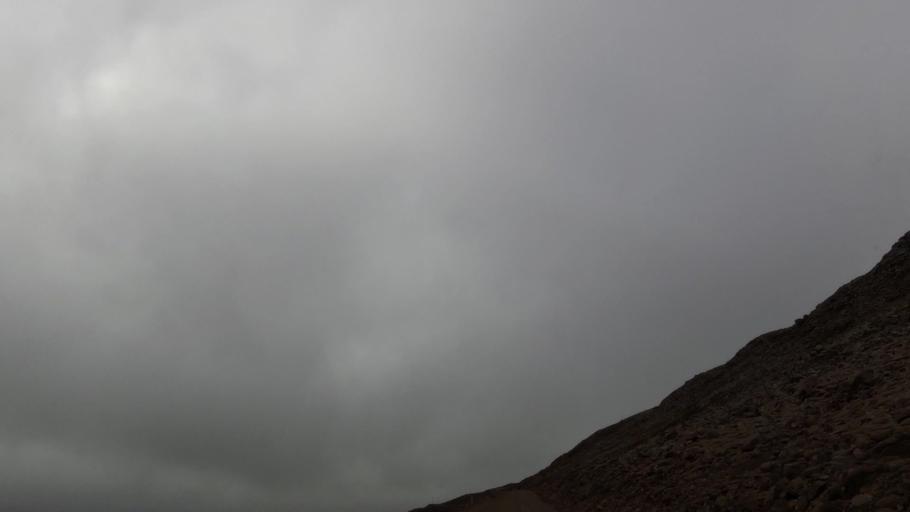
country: IS
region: West
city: Olafsvik
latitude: 65.5257
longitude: -24.4224
